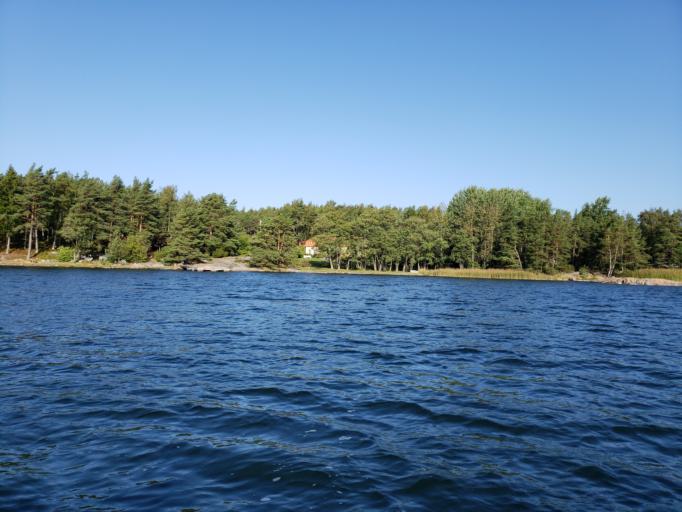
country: FI
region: Varsinais-Suomi
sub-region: Aboland-Turunmaa
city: Dragsfjaerd
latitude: 59.9099
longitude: 22.3765
